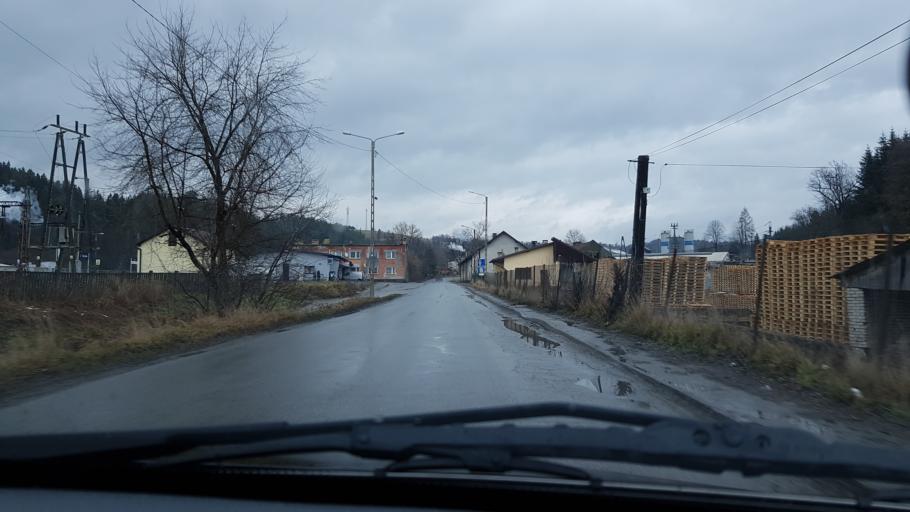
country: PL
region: Lesser Poland Voivodeship
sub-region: Powiat suski
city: Jordanow
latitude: 49.6363
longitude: 19.8313
